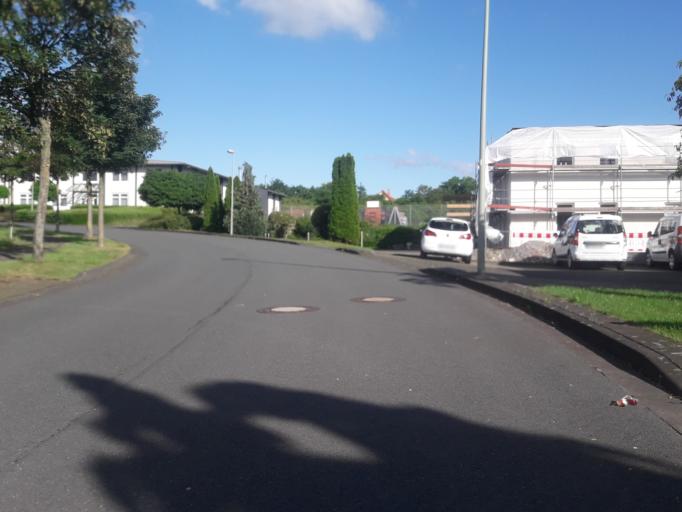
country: DE
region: North Rhine-Westphalia
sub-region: Regierungsbezirk Detmold
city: Paderborn
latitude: 51.7232
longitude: 8.7950
